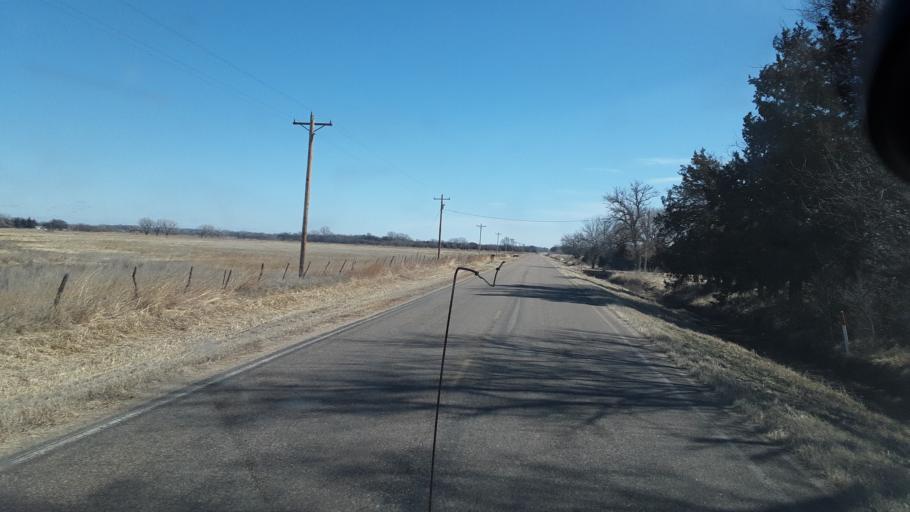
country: US
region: Kansas
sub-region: Reno County
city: Nickerson
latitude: 38.2174
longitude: -98.0773
